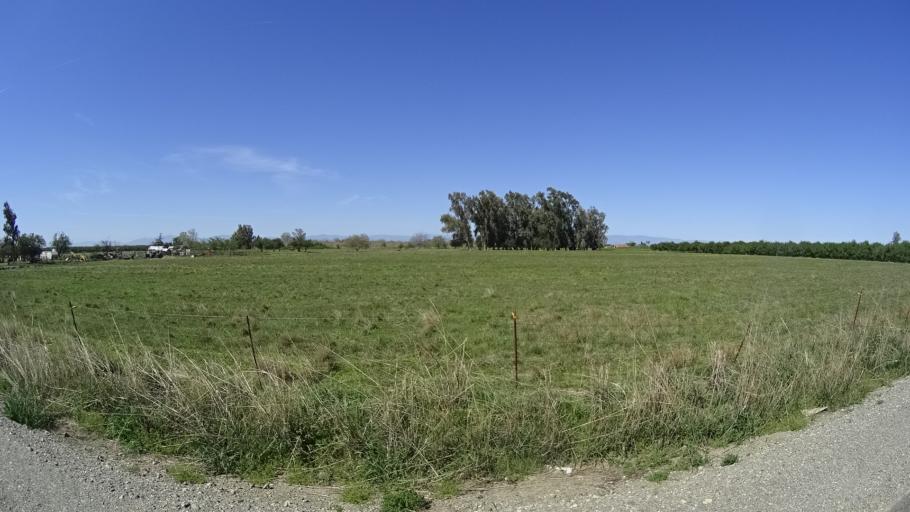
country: US
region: California
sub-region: Glenn County
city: Orland
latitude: 39.7350
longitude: -122.1409
